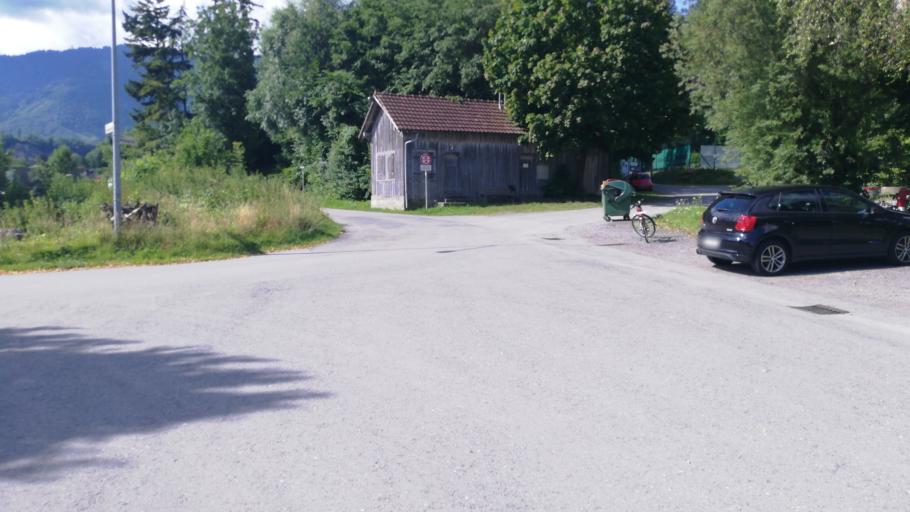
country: AT
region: Vorarlberg
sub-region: Politischer Bezirk Feldkirch
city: Nofels
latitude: 47.2518
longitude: 9.5806
